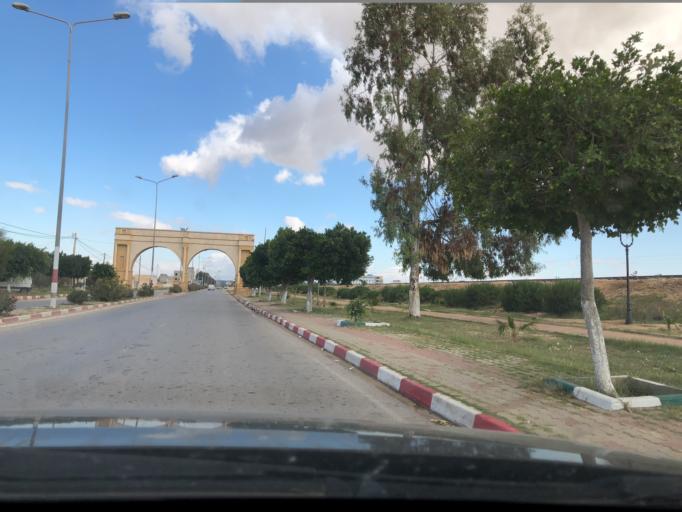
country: TN
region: Al Qasrayn
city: Kasserine
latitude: 35.1817
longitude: 8.8582
